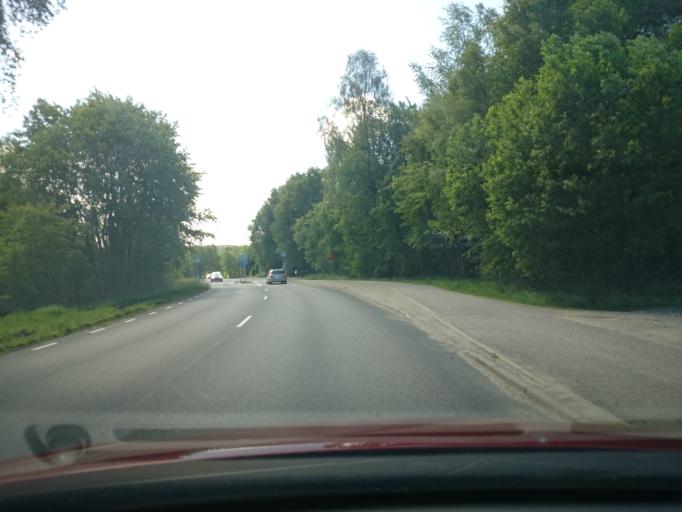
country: SE
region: Vaestra Goetaland
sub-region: Harryda Kommun
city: Landvetter
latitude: 57.6922
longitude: 12.2063
